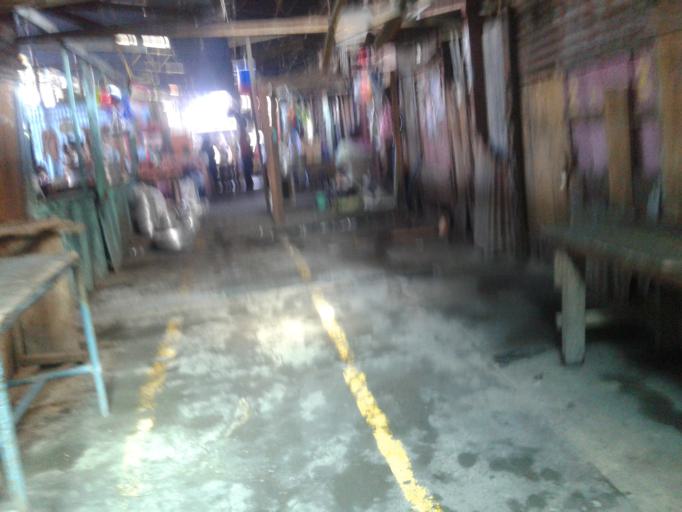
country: NI
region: Managua
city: Managua
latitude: 12.1488
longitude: -86.2599
